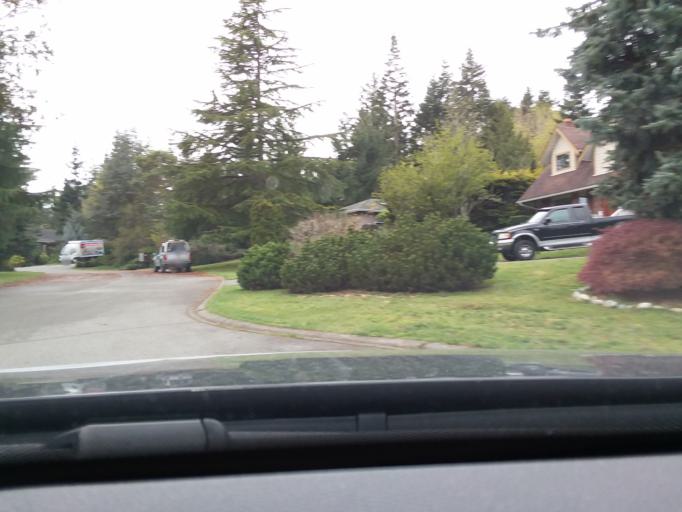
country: CA
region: British Columbia
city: North Saanich
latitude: 48.6153
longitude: -123.4231
